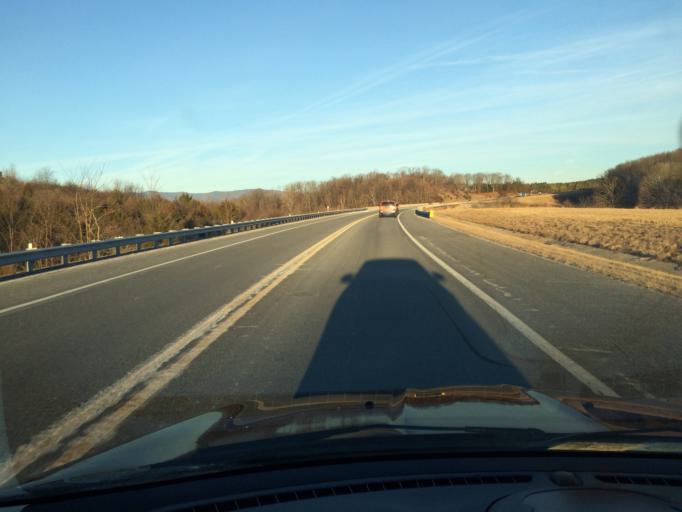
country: US
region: Virginia
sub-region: City of Staunton
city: Staunton
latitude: 38.1401
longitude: -79.1092
